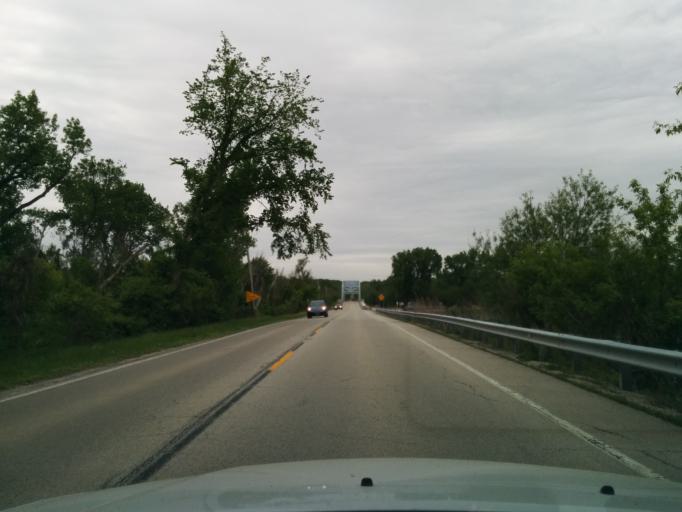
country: US
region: Illinois
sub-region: Cook County
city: Palos Park
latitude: 41.6911
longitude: -87.8750
